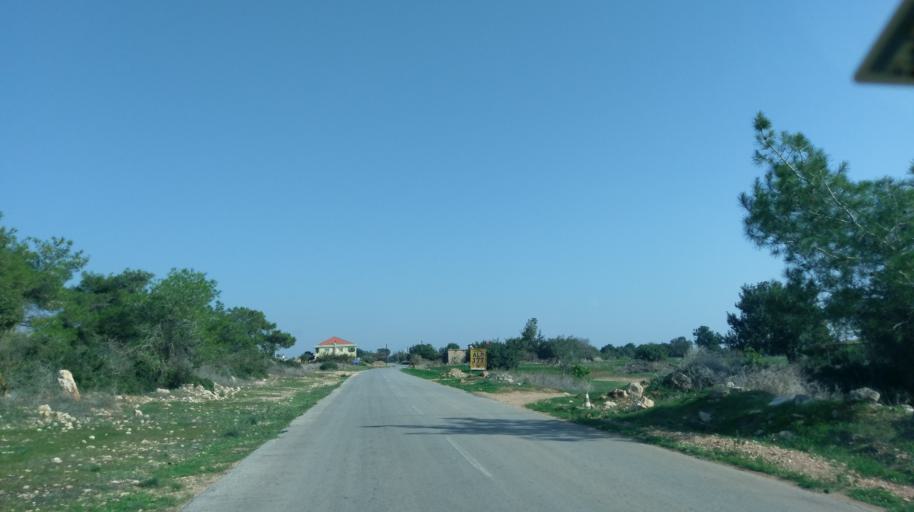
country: CY
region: Ammochostos
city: Leonarisso
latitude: 35.4808
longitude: 34.1757
